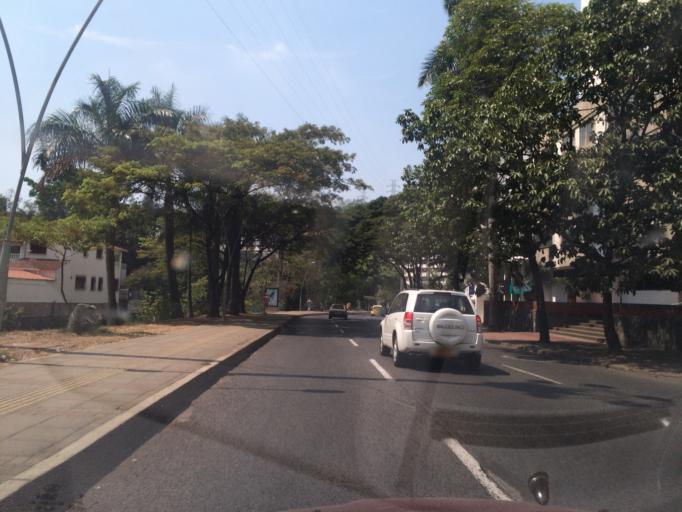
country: CO
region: Valle del Cauca
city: Cali
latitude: 3.4528
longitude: -76.5464
